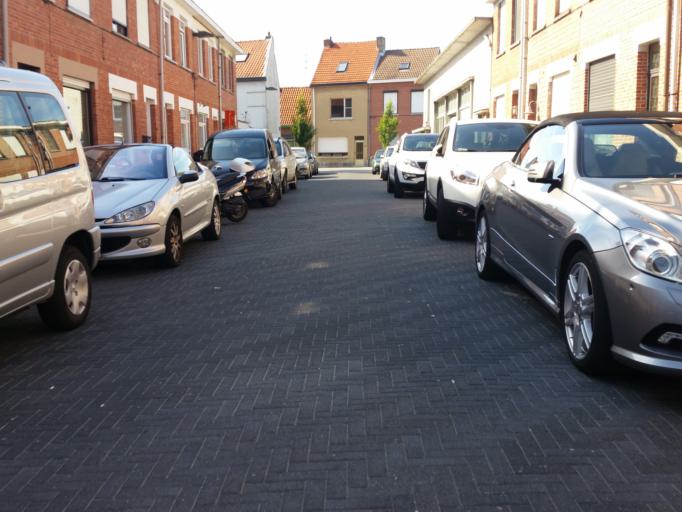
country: BE
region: Flanders
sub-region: Provincie Antwerpen
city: Mechelen
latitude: 51.0407
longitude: 4.4635
